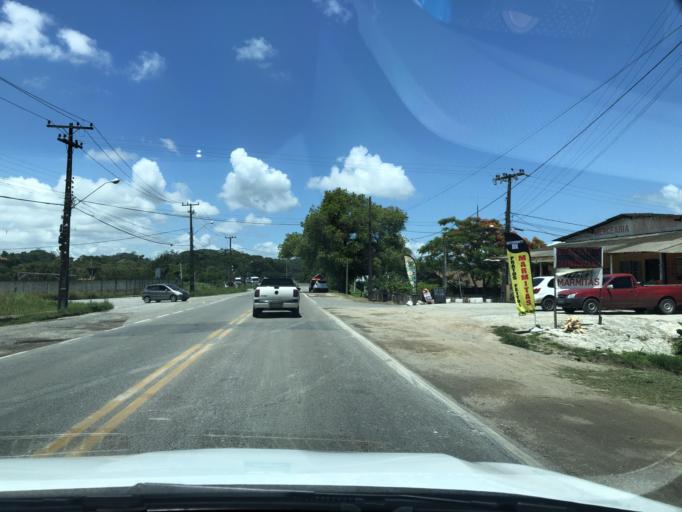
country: BR
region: Santa Catarina
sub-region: Sao Francisco Do Sul
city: Sao Francisco do Sul
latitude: -26.2498
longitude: -48.6084
